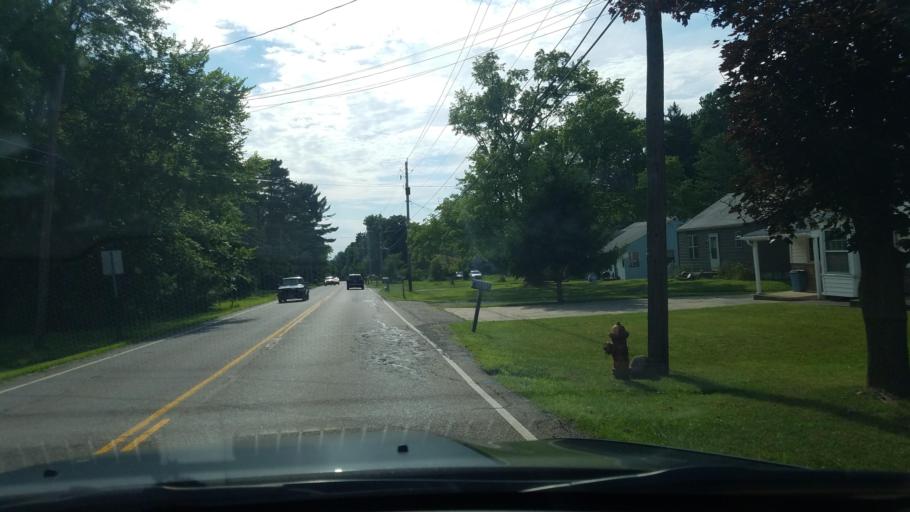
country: US
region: Ohio
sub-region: Trumbull County
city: McKinley Heights
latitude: 41.1844
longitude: -80.6954
